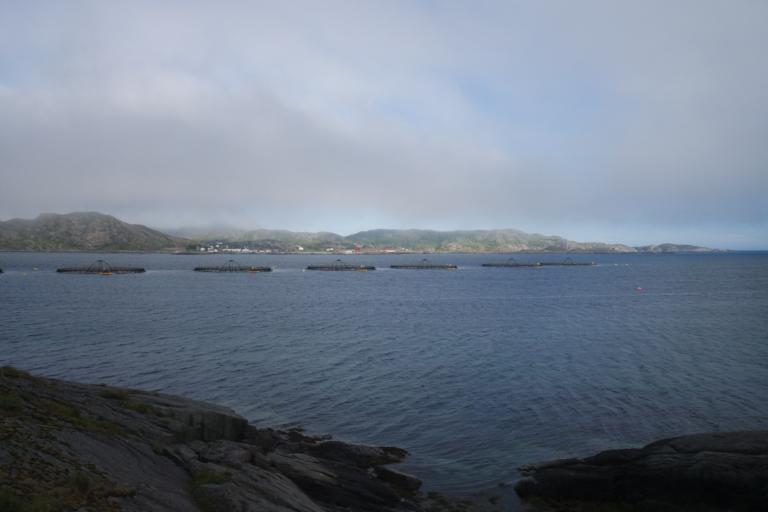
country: NO
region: Nordland
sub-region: Flakstad
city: Ramberg
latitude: 68.0043
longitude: 13.1763
